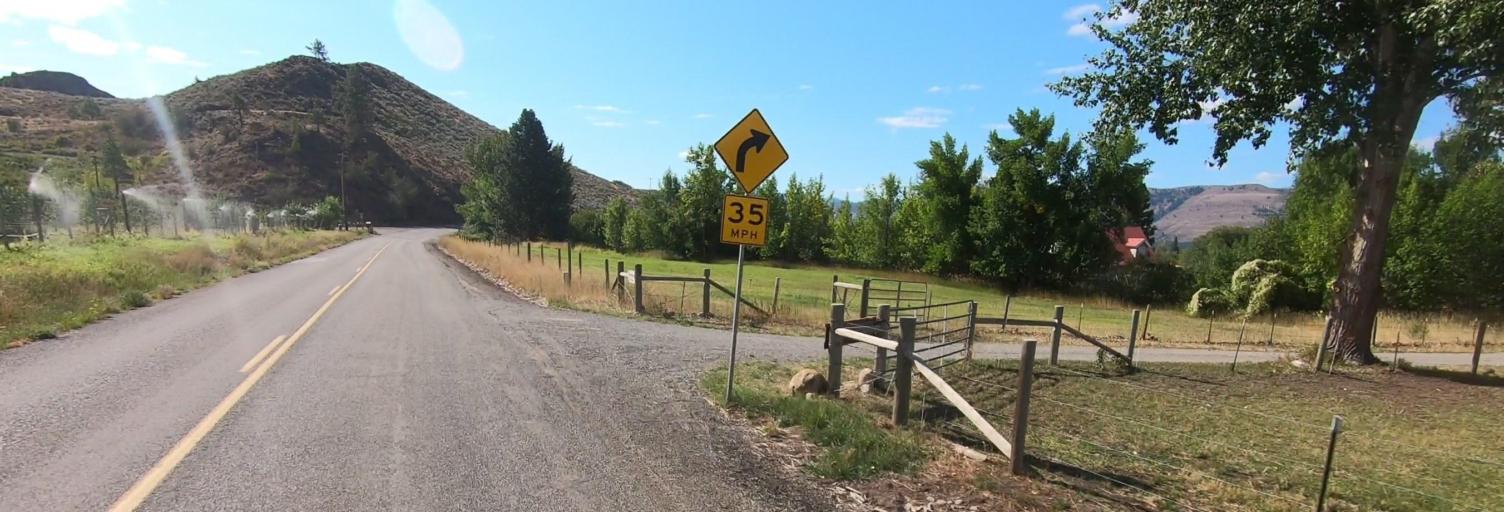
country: US
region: Washington
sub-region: Okanogan County
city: Brewster
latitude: 48.5104
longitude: -120.1762
